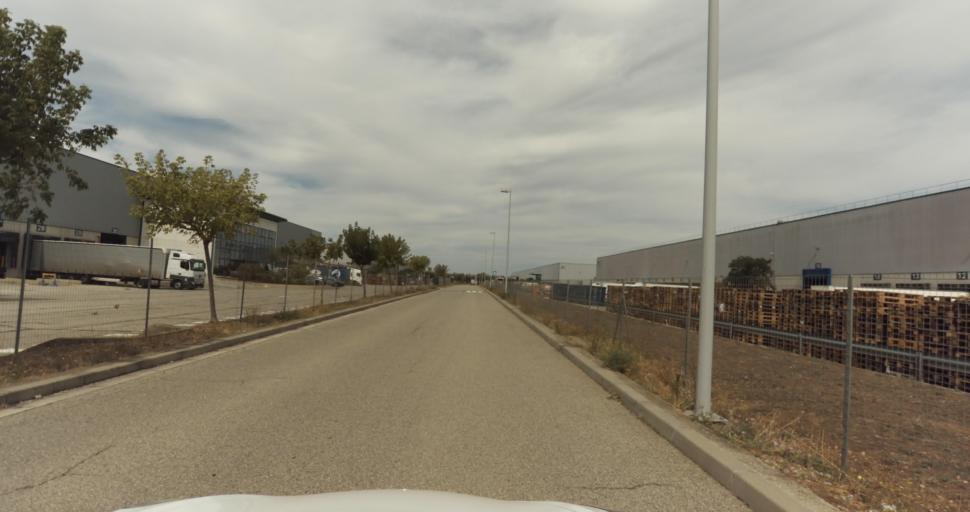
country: FR
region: Provence-Alpes-Cote d'Azur
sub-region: Departement des Bouches-du-Rhone
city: Miramas
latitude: 43.6076
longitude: 4.9990
